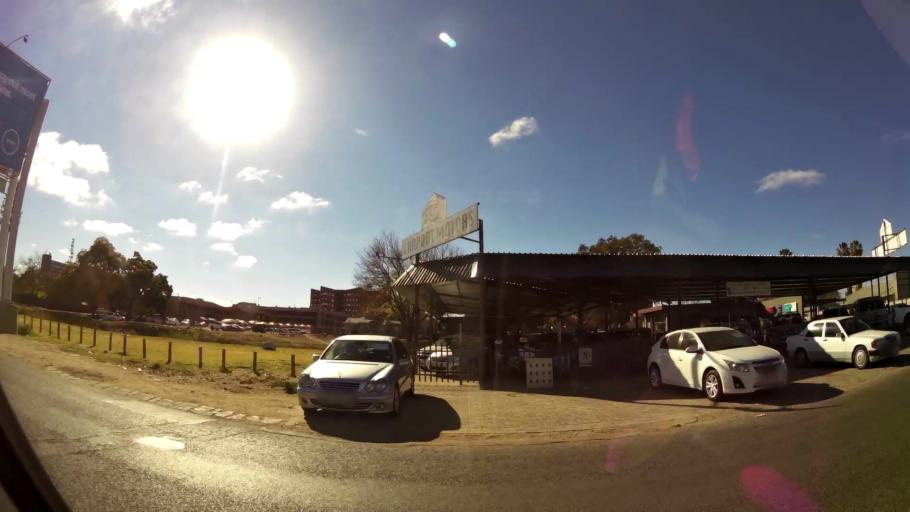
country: ZA
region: Limpopo
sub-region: Capricorn District Municipality
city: Polokwane
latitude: -23.9168
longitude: 29.4515
